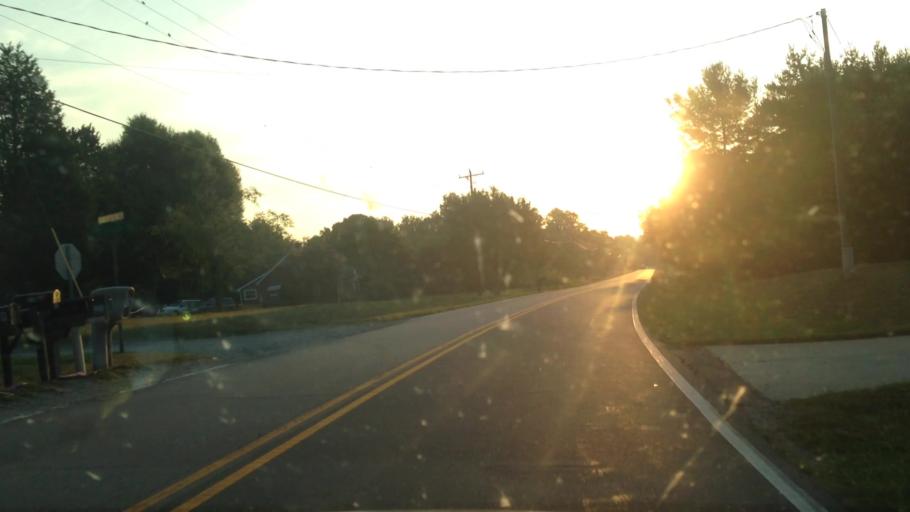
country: US
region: North Carolina
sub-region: Forsyth County
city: Walkertown
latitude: 36.1571
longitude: -80.1231
